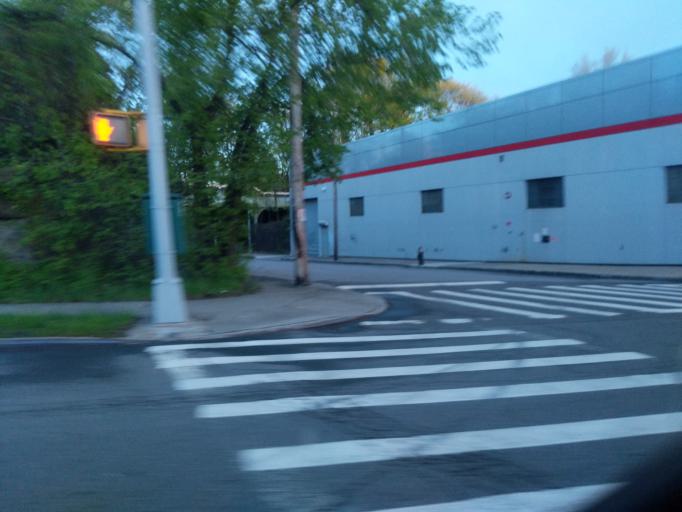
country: US
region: New York
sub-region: Bronx
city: Eastchester
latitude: 40.8822
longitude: -73.8365
